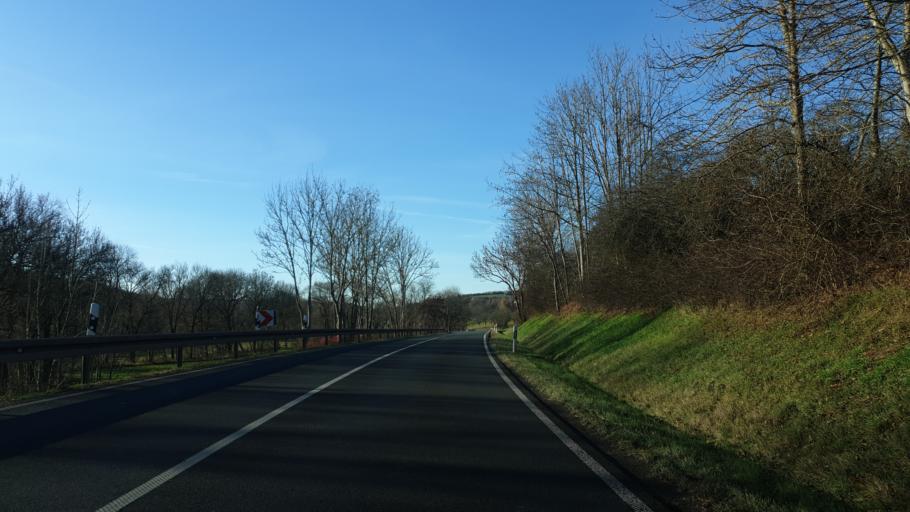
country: DE
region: Thuringia
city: Hartmannsdorf
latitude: 50.9575
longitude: 11.9648
